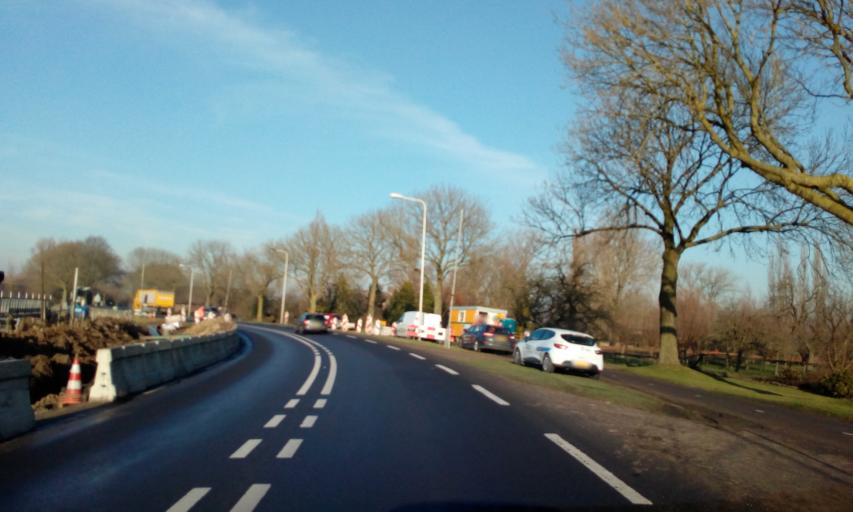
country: NL
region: Utrecht
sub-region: Gemeente Montfoort
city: Montfoort
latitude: 52.0534
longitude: 4.9276
